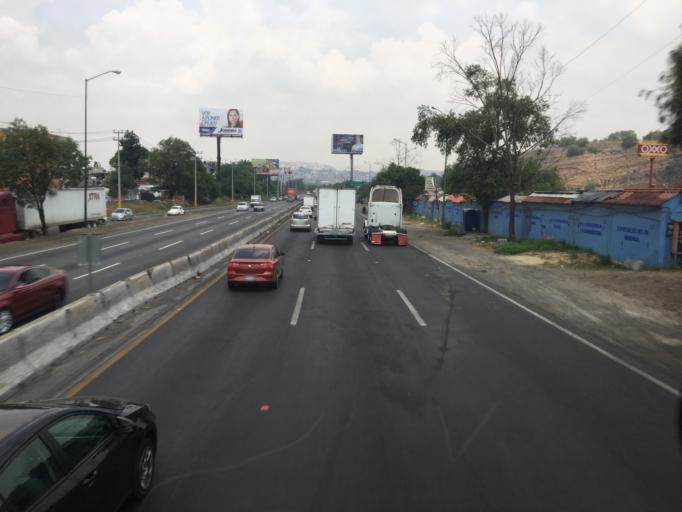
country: MX
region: Mexico
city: Tlalnepantla
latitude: 19.5593
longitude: -99.1870
